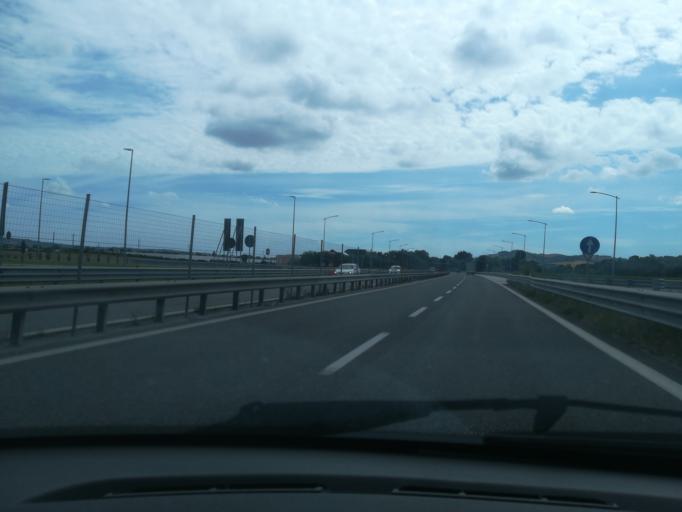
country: IT
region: The Marches
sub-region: Provincia di Macerata
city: Villa San Filippo
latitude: 43.2626
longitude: 13.5624
